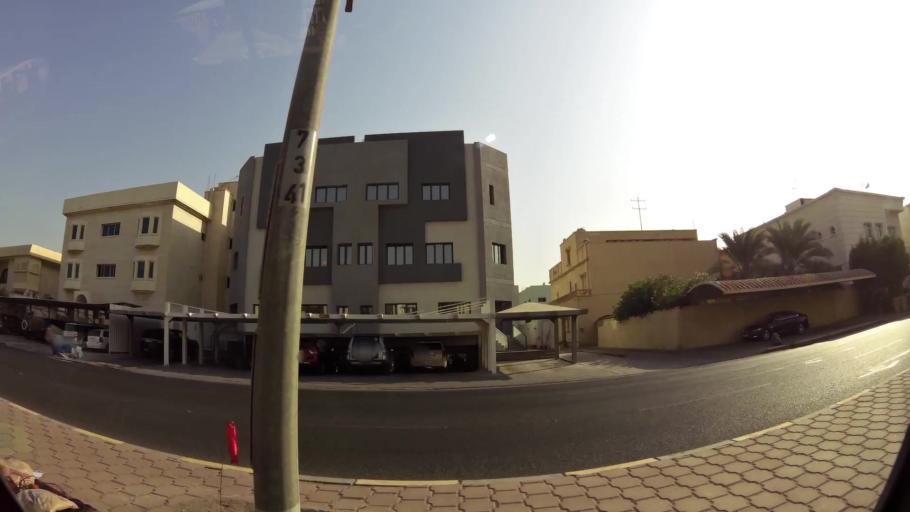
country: KW
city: Bayan
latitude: 29.3154
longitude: 48.0393
